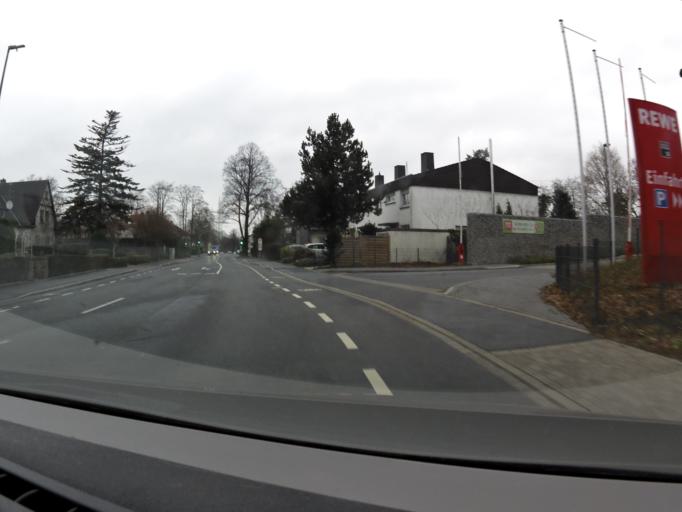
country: DE
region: North Rhine-Westphalia
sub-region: Regierungsbezirk Arnsberg
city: Dortmund
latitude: 51.4612
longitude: 7.4797
